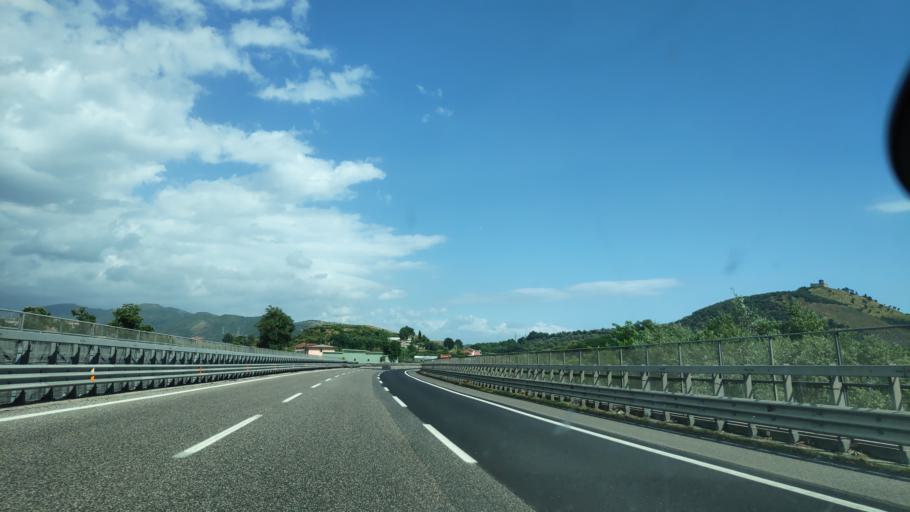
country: IT
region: Campania
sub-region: Provincia di Salerno
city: San Mango Piemonte
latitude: 40.6861
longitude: 14.8497
